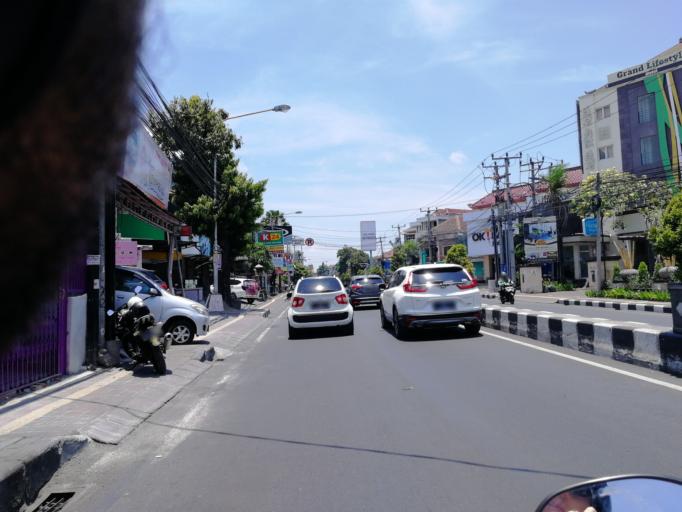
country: ID
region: Bali
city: Karyadharma
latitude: -8.6786
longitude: 115.2050
